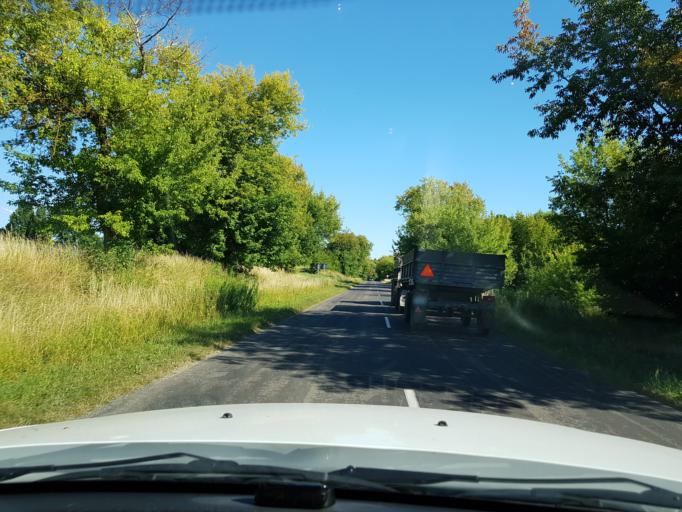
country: PL
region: West Pomeranian Voivodeship
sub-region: Powiat lobeski
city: Lobez
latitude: 53.7028
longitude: 15.6022
